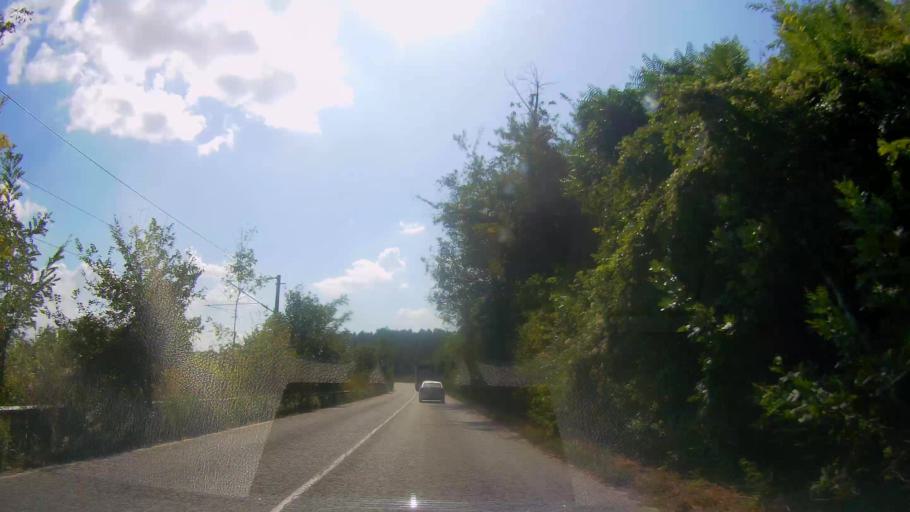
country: BG
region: Veliko Turnovo
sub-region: Obshtina Polski Trumbesh
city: Polski Trumbesh
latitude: 43.4354
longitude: 25.6551
